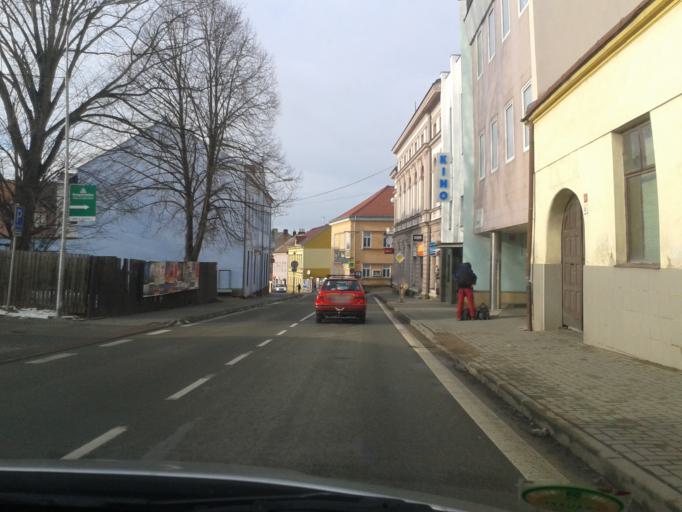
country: CZ
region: South Moravian
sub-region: Okres Blansko
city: Boskovice
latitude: 49.4881
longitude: 16.6618
